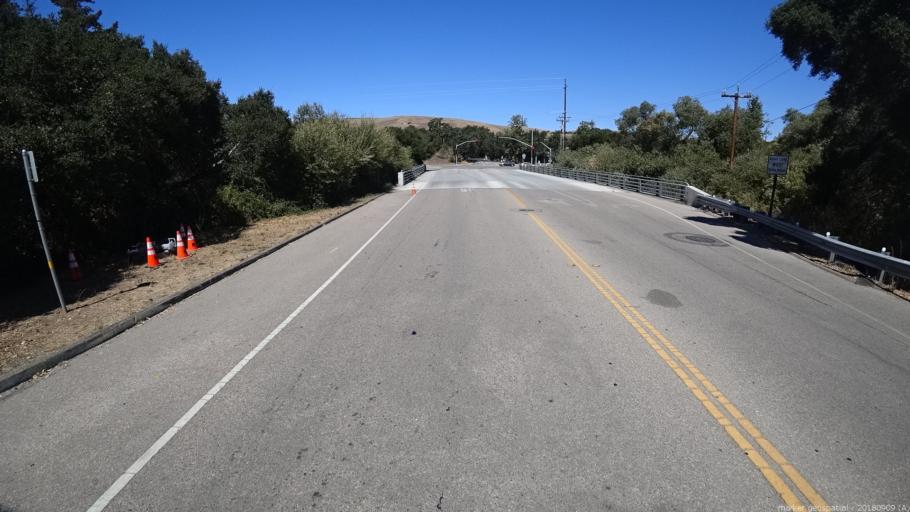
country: US
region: California
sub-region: Monterey County
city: Carmel Valley Village
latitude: 36.5791
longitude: -121.7202
